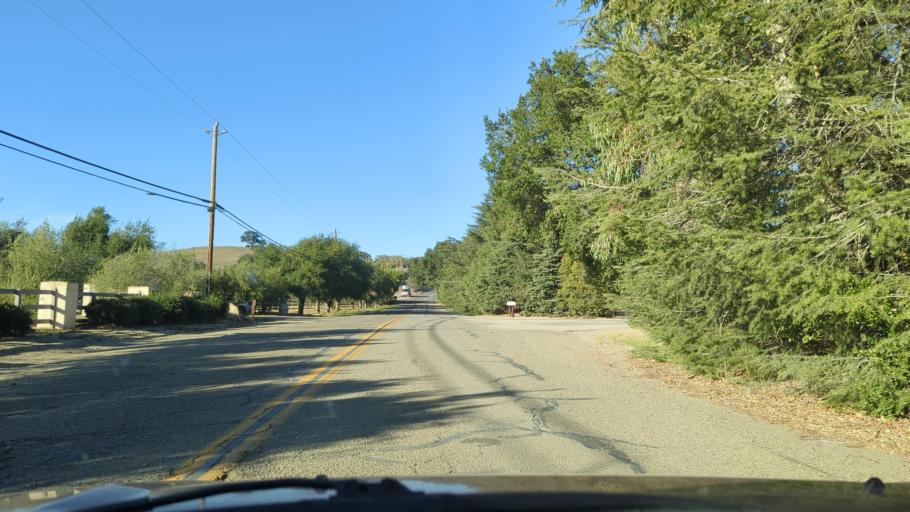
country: US
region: California
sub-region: Santa Barbara County
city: Santa Ynez
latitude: 34.5876
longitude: -120.0996
